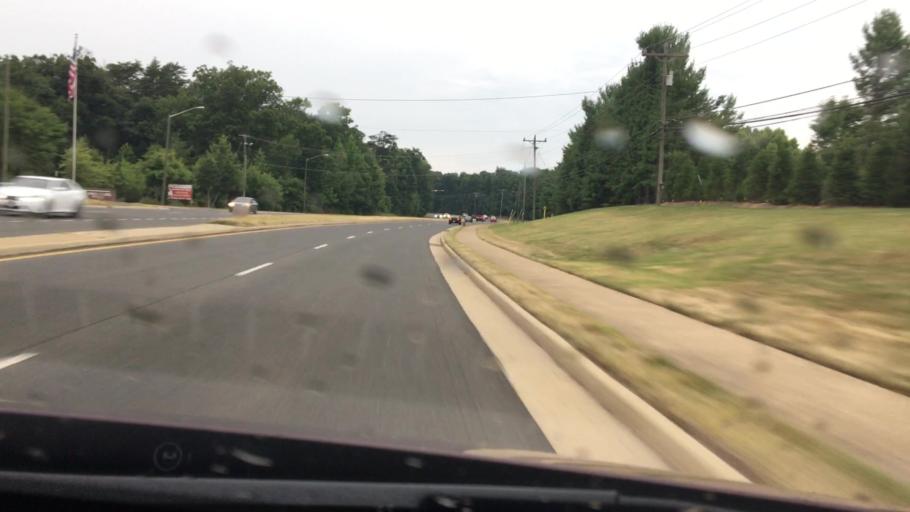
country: US
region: Virginia
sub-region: Fairfax County
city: Centreville
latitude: 38.8294
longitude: -77.3925
